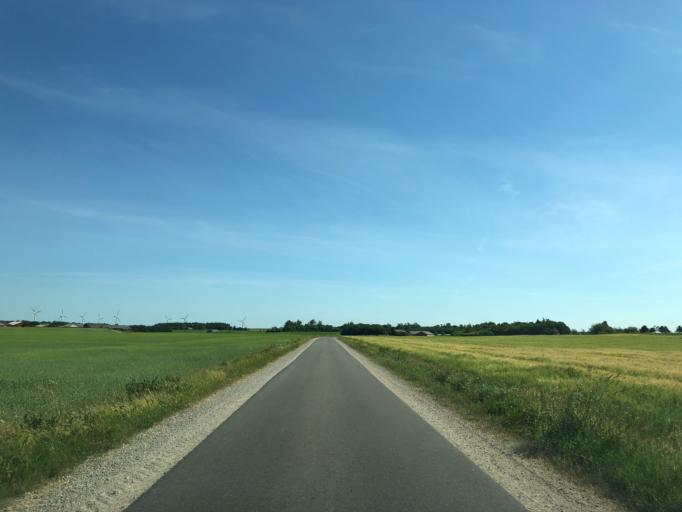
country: DK
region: Central Jutland
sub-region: Struer Kommune
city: Struer
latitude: 56.4292
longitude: 8.4631
